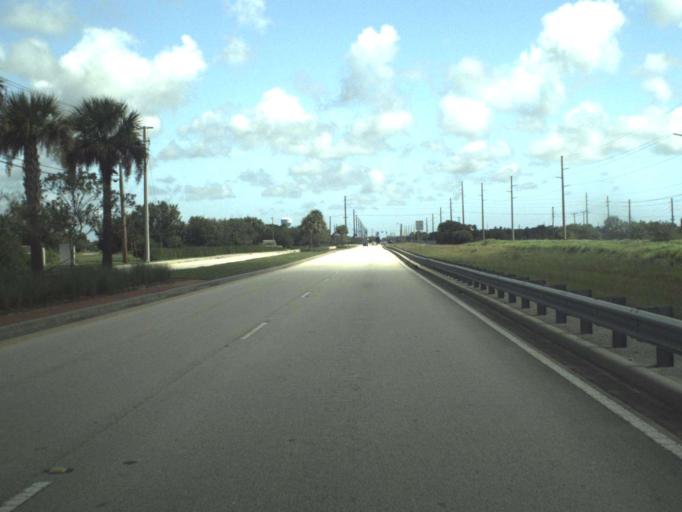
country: US
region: Florida
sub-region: Indian River County
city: Vero Beach South
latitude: 27.6196
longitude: -80.4470
